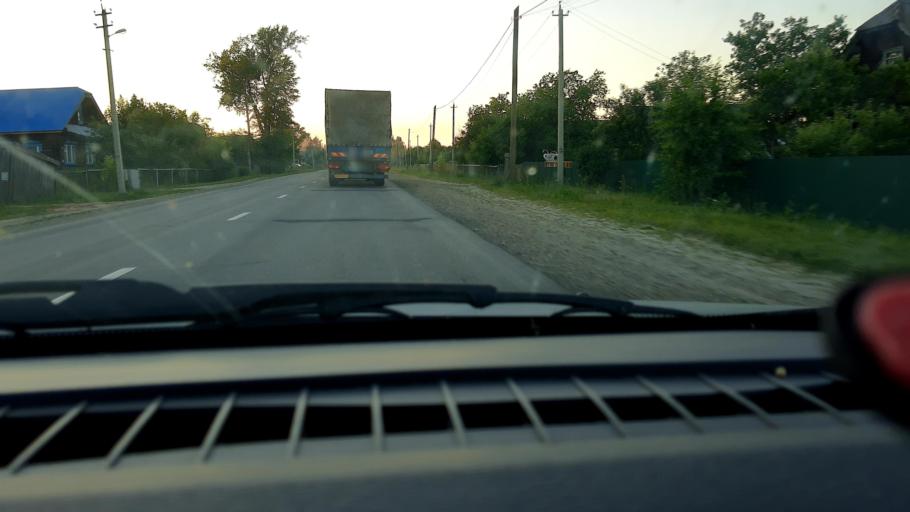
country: RU
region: Nizjnij Novgorod
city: Uren'
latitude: 57.3408
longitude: 45.7113
